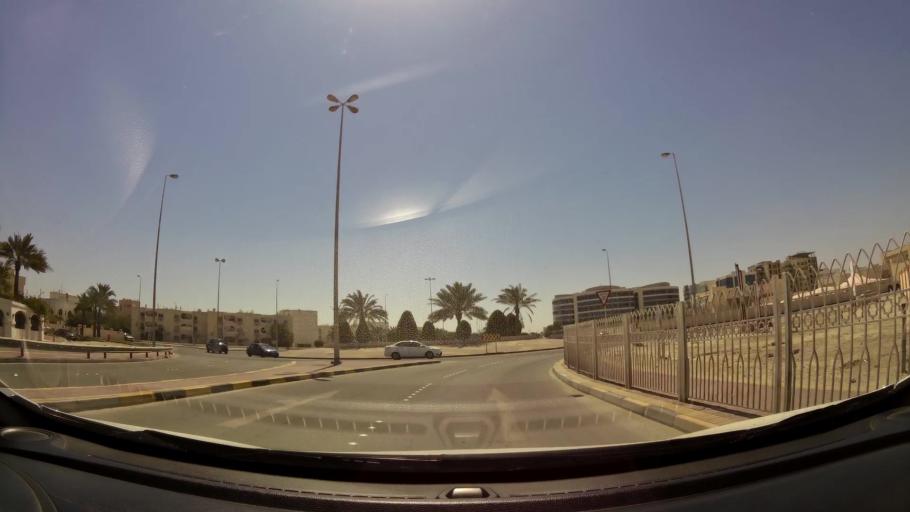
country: BH
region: Muharraq
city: Al Muharraq
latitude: 26.2672
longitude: 50.6031
